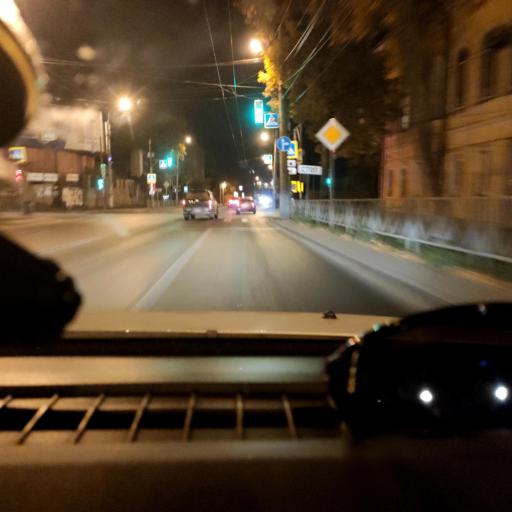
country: RU
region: Samara
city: Rozhdestveno
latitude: 53.1782
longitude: 50.0752
